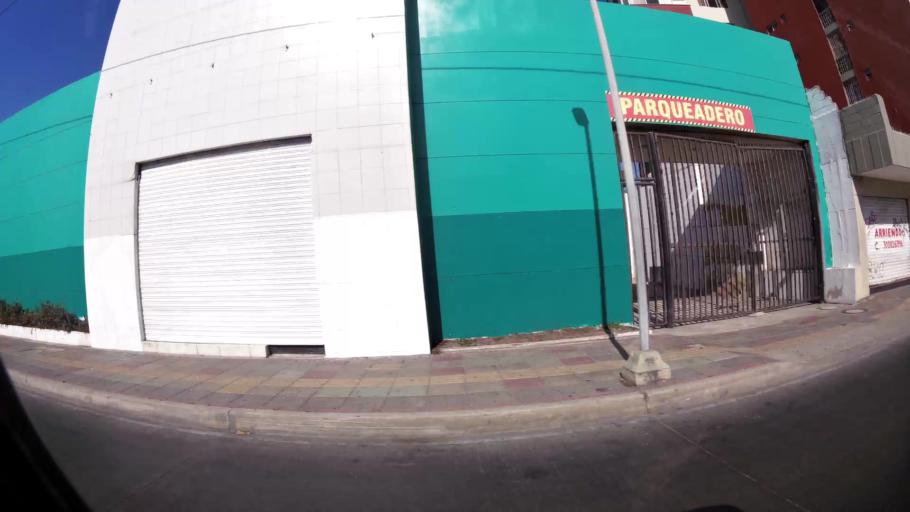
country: CO
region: Atlantico
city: Barranquilla
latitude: 10.9838
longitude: -74.7860
